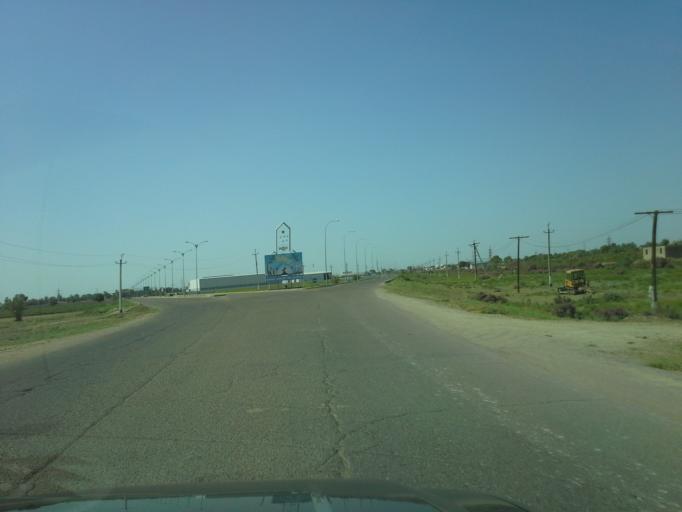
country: TM
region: Dasoguz
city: Dasoguz
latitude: 41.8078
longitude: 60.0042
